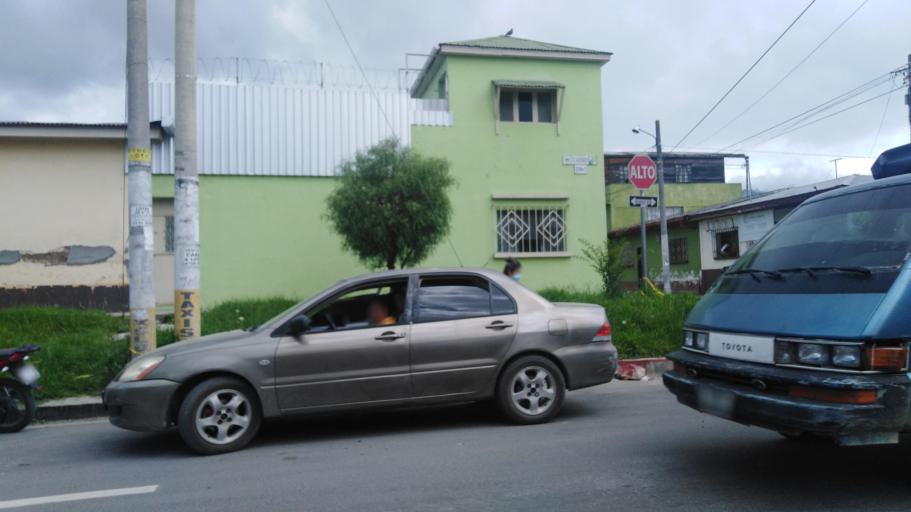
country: GT
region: Quetzaltenango
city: Quetzaltenango
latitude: 14.8462
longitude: -91.5133
